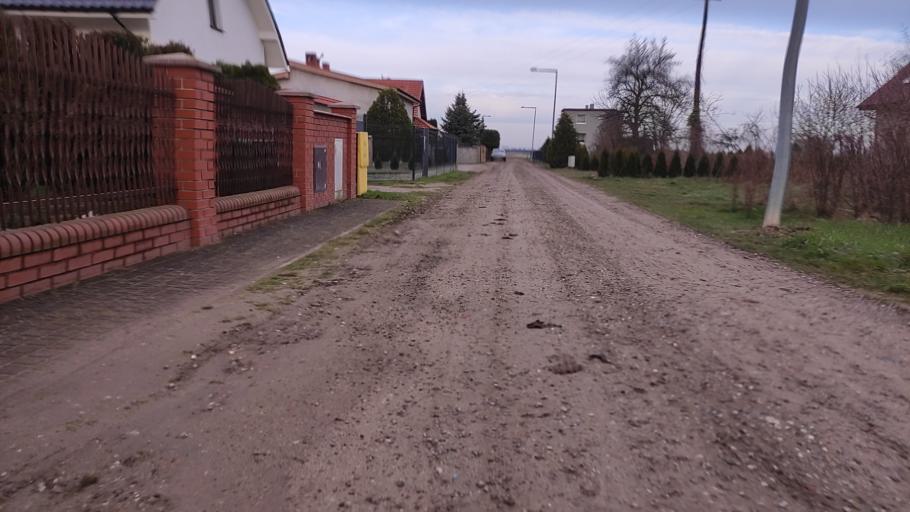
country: PL
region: Greater Poland Voivodeship
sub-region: Powiat poznanski
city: Swarzedz
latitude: 52.4007
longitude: 17.1529
